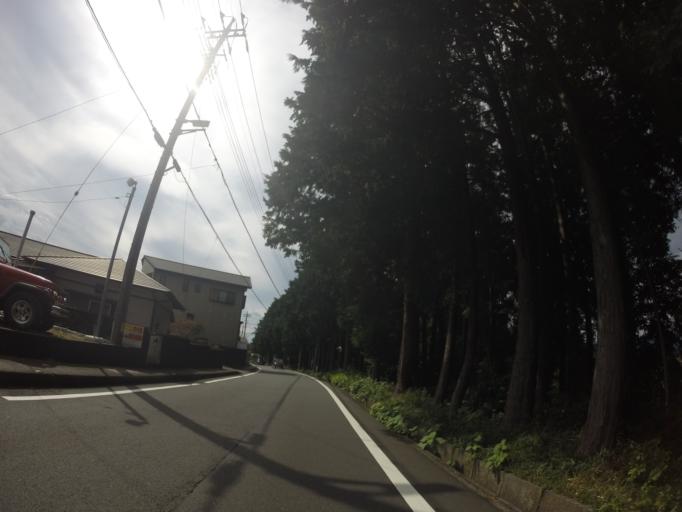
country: JP
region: Shizuoka
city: Fuji
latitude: 35.2083
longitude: 138.6711
